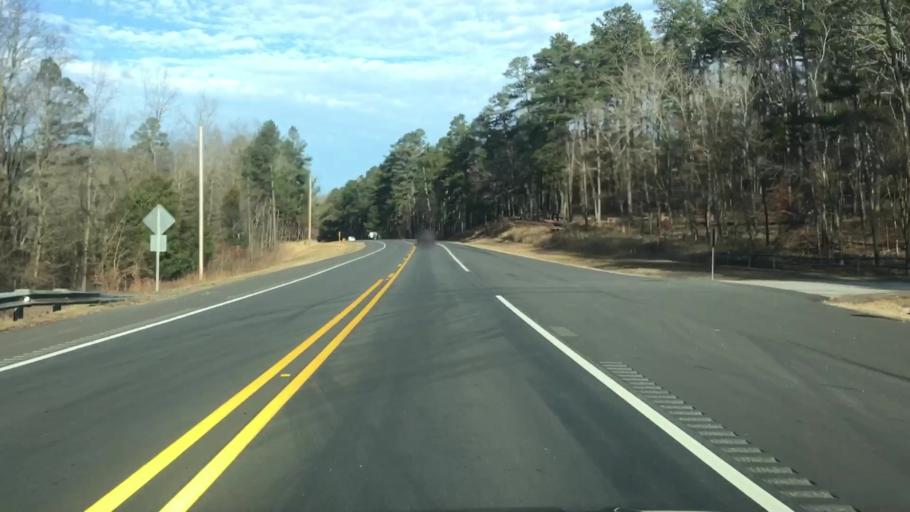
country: US
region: Arkansas
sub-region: Pike County
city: Glenwood
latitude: 34.5158
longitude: -93.3839
